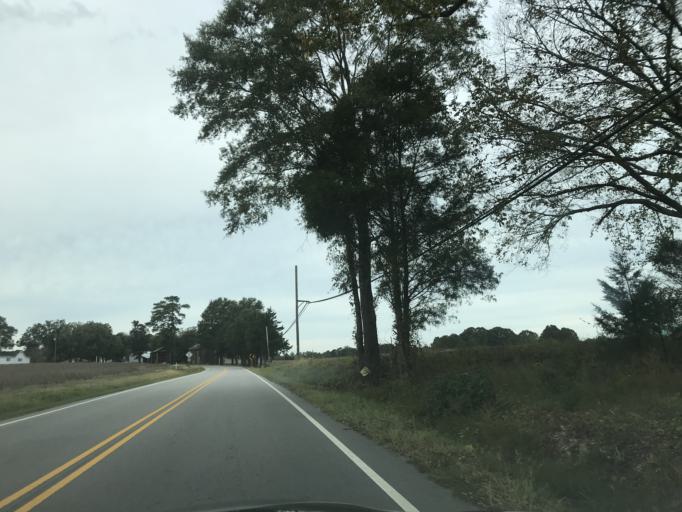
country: US
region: North Carolina
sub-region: Wake County
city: Knightdale
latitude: 35.8238
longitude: -78.5050
